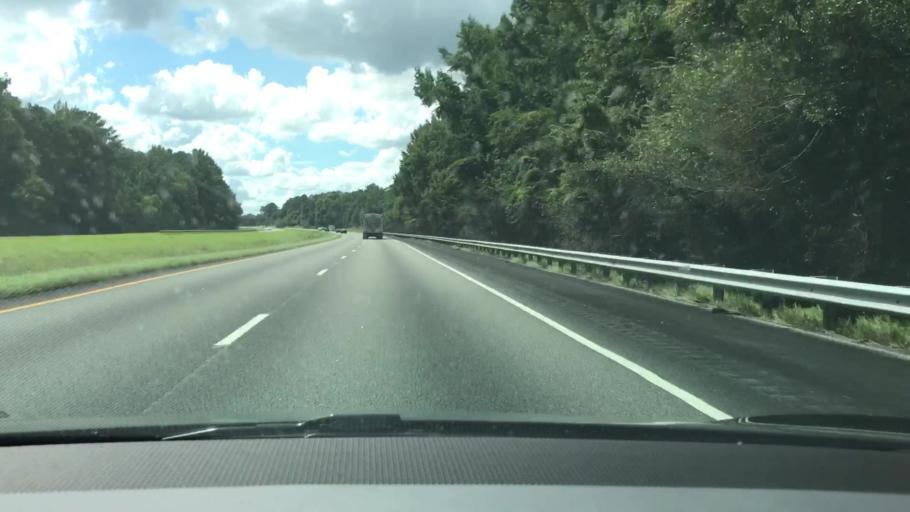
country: US
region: Alabama
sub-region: Elmore County
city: Tallassee
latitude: 32.4382
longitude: -85.8647
